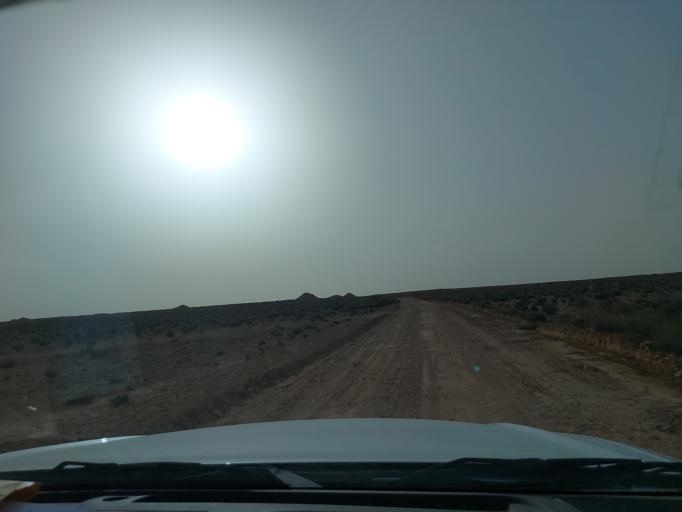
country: TN
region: Madanin
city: Medenine
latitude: 33.2859
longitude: 10.5964
